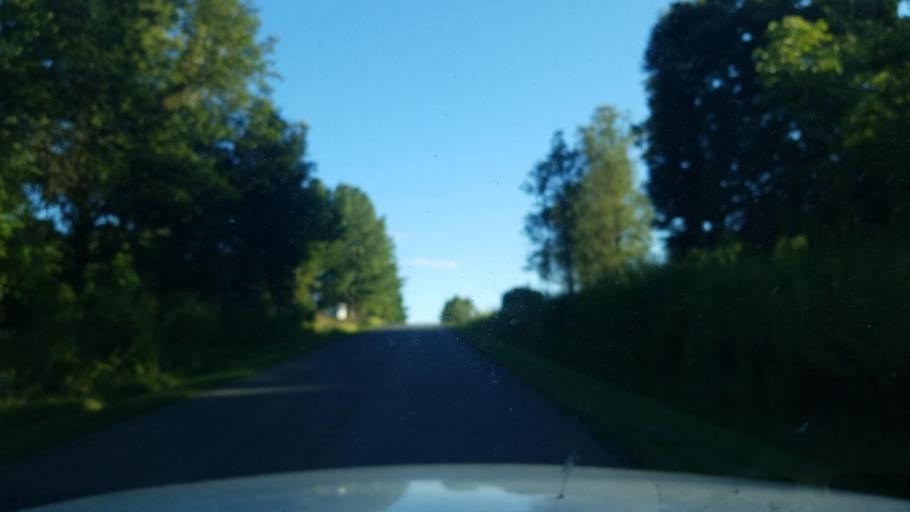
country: US
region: Illinois
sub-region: Hardin County
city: Elizabethtown
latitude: 37.5854
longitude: -88.3655
